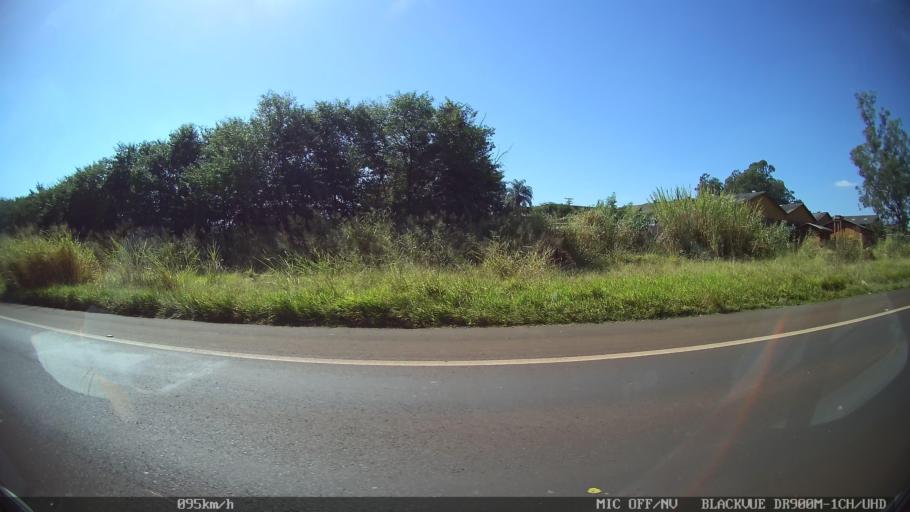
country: BR
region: Sao Paulo
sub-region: Franca
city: Franca
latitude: -20.5531
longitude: -47.4506
